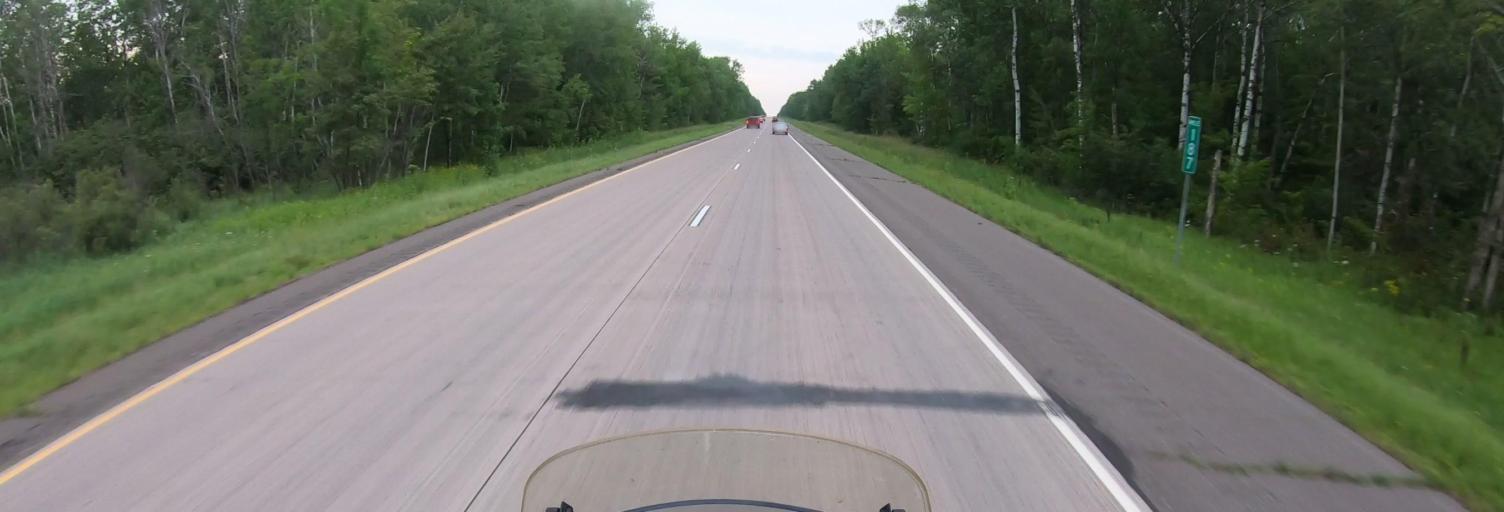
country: US
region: Minnesota
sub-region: Pine County
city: Hinckley
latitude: 46.0647
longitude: -92.9066
